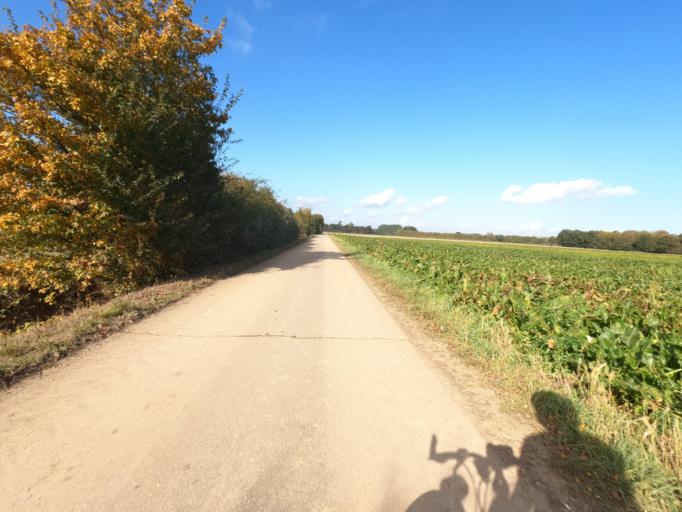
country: DE
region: North Rhine-Westphalia
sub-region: Regierungsbezirk Koln
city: Inden
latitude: 50.8684
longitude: 6.4109
